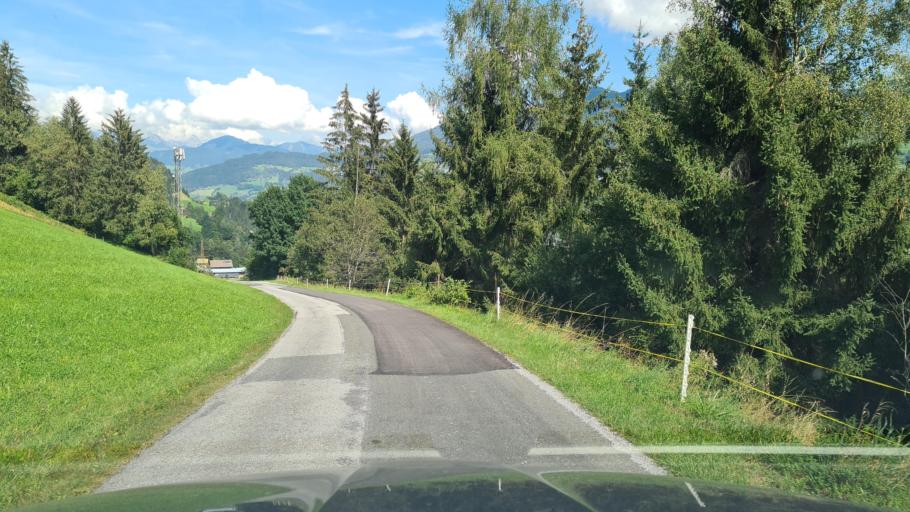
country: AT
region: Salzburg
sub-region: Politischer Bezirk Sankt Johann im Pongau
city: Sankt Johann im Pongau
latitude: 47.3550
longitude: 13.1856
